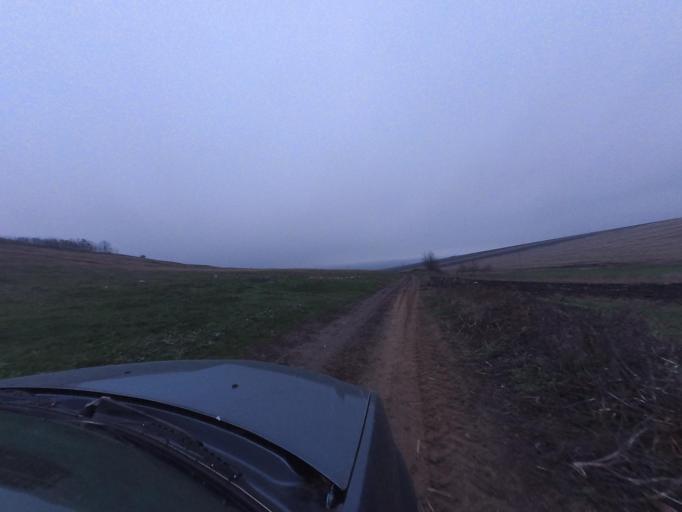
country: RO
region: Galati
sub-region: Comuna Balabanesti
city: Balabanesti
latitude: 46.1336
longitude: 27.7501
